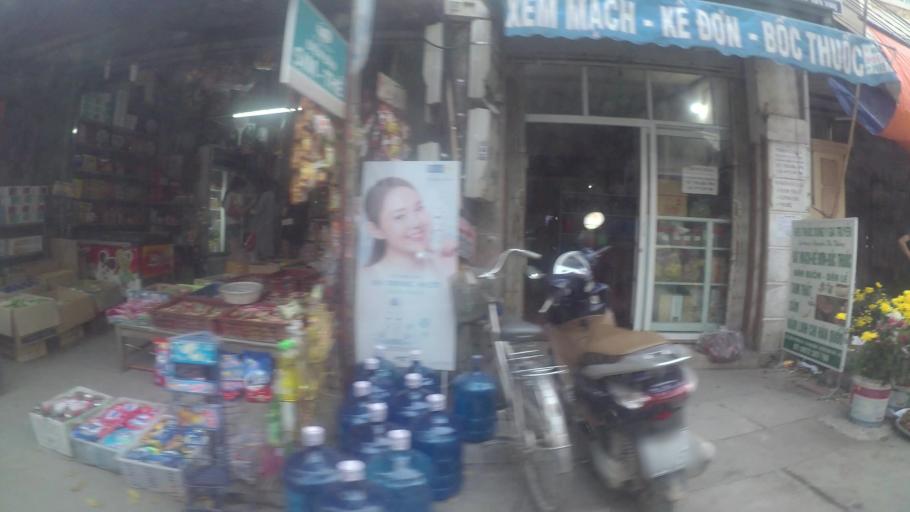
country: VN
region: Ha Noi
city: Ha Dong
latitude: 20.9950
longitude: 105.7296
